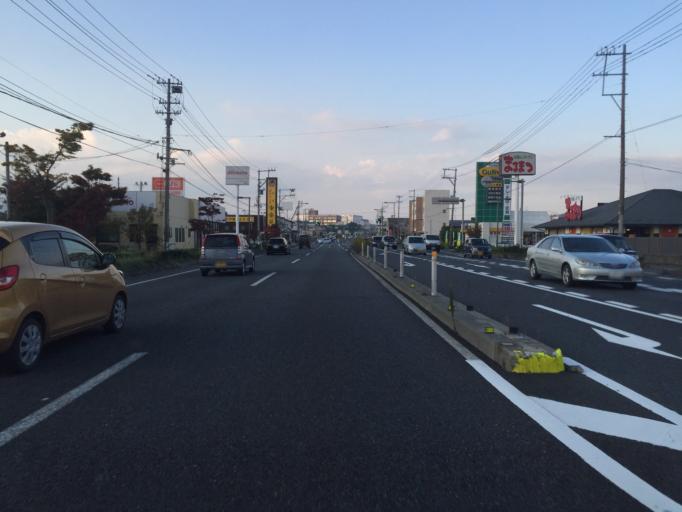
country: JP
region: Fukushima
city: Motomiya
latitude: 37.5140
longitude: 140.3952
